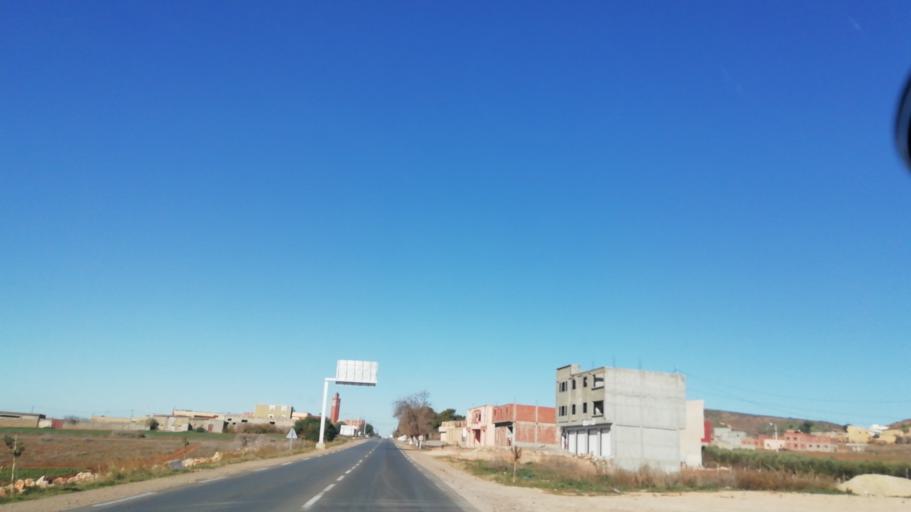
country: DZ
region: Tlemcen
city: Nedroma
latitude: 34.8832
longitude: -1.9027
